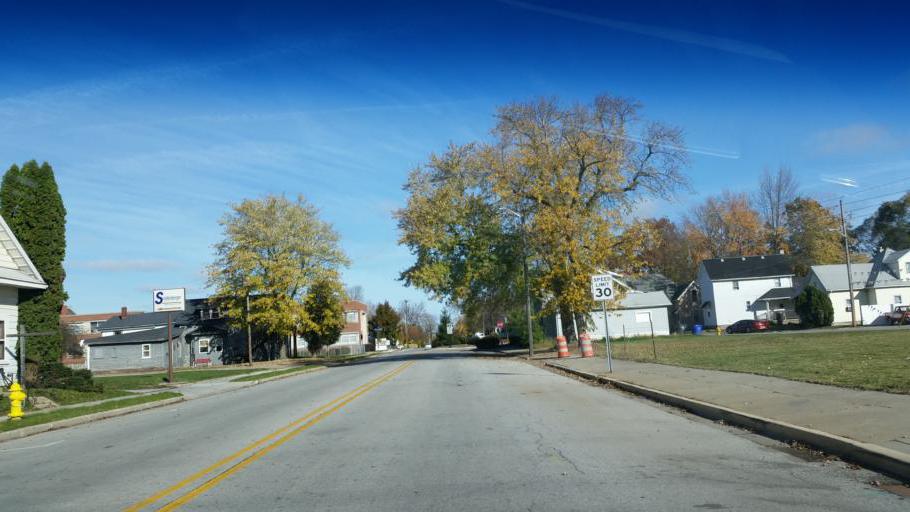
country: US
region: Indiana
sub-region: Howard County
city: Kokomo
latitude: 40.4767
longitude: -86.1298
